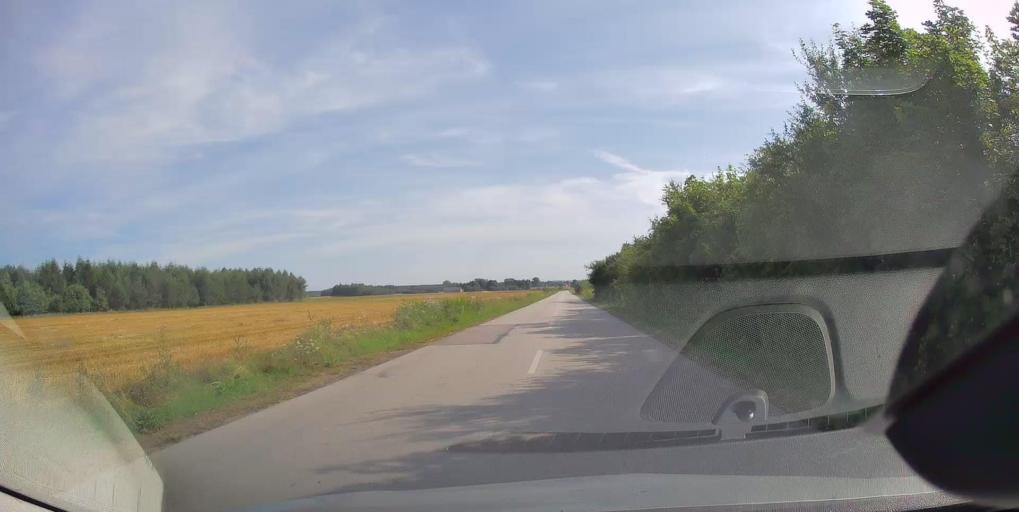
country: PL
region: Lodz Voivodeship
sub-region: Powiat opoczynski
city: Mniszkow
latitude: 51.3653
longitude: 20.0383
